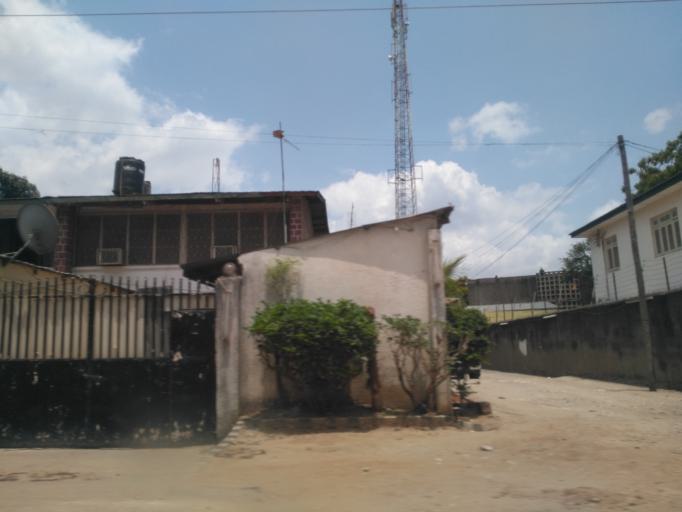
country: TZ
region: Dar es Salaam
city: Dar es Salaam
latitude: -6.8043
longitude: 39.2746
